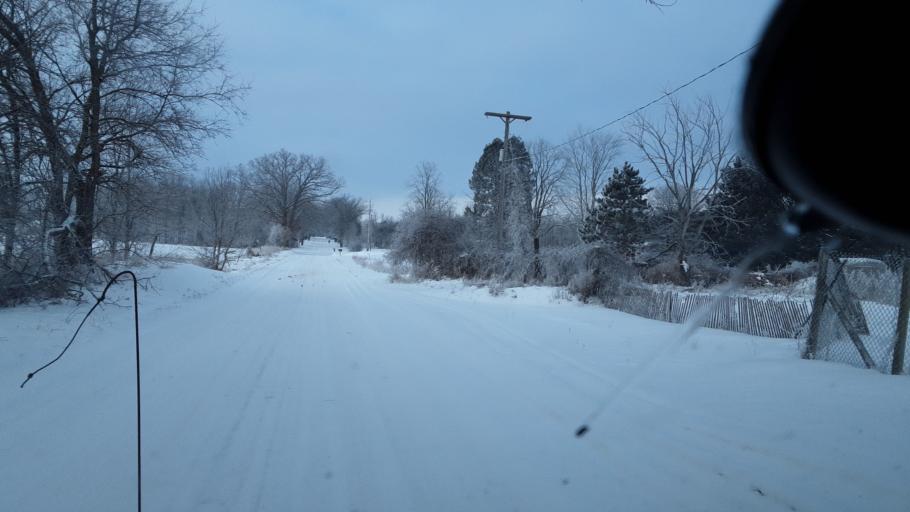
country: US
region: Michigan
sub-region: Ingham County
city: Leslie
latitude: 42.4221
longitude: -84.4891
